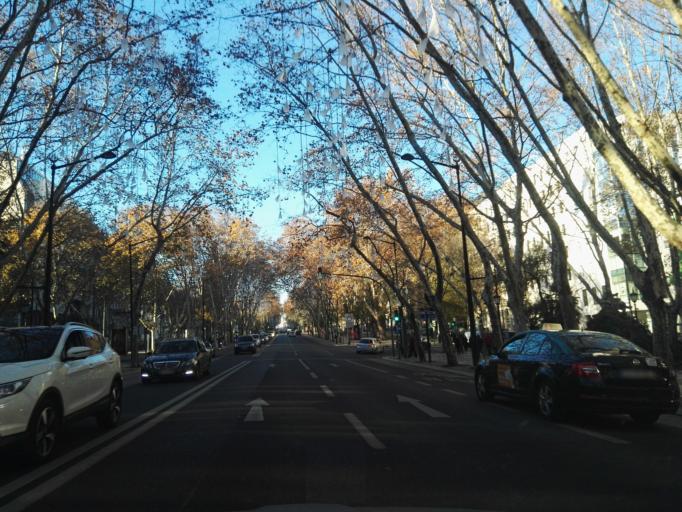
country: PT
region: Lisbon
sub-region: Lisbon
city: Lisbon
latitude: 38.7180
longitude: -9.1435
